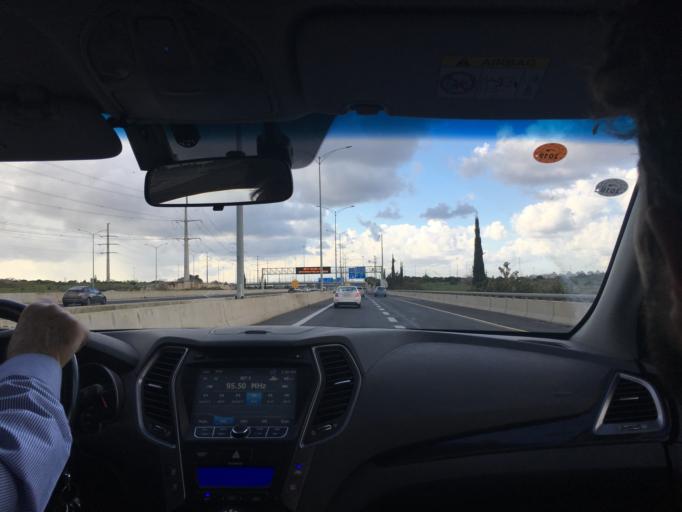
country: IL
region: Central District
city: Rishon LeZiyyon
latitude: 31.9509
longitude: 34.7959
